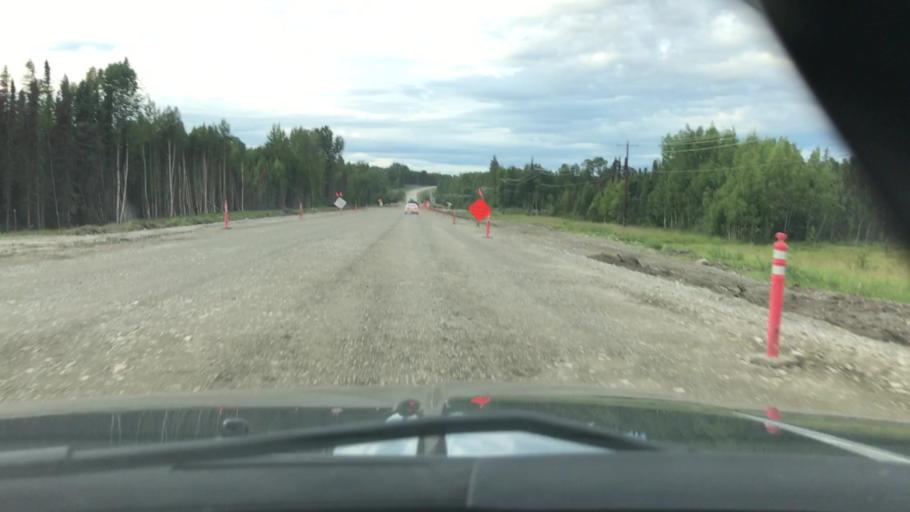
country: US
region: Alaska
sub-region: Matanuska-Susitna Borough
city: Y
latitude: 62.0975
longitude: -150.0614
